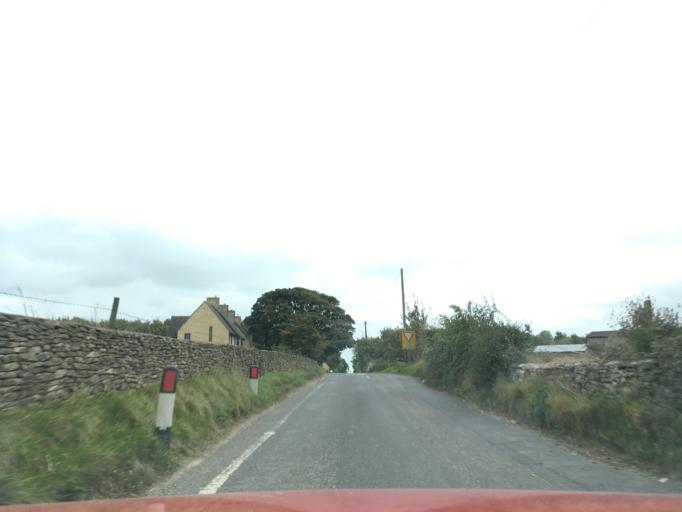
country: GB
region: England
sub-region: South Gloucestershire
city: Horton
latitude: 51.5735
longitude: -2.3065
